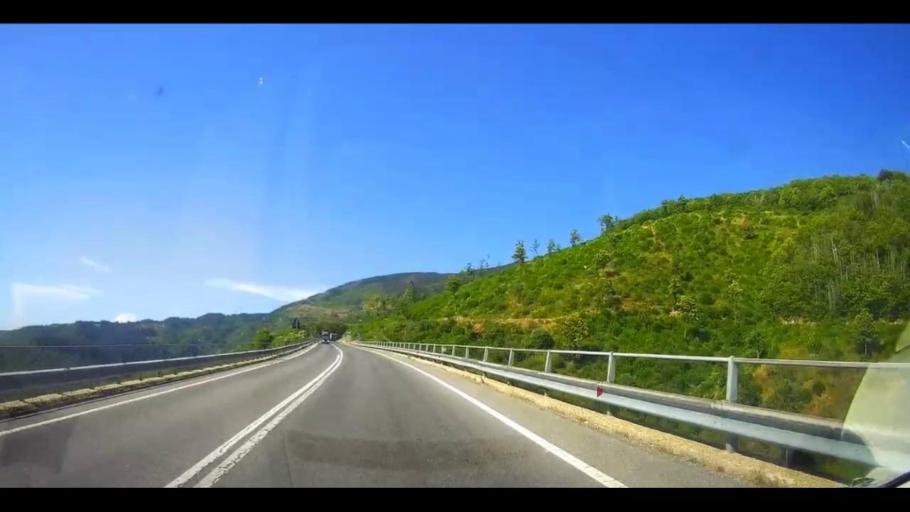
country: IT
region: Calabria
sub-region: Provincia di Cosenza
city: Celico
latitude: 39.3066
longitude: 16.3540
